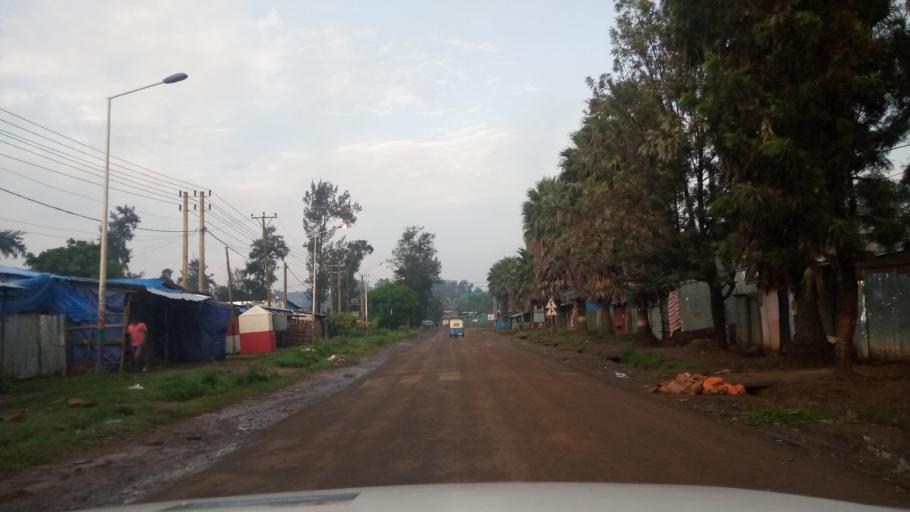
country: ET
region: Oromiya
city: Jima
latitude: 7.6821
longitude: 36.8419
